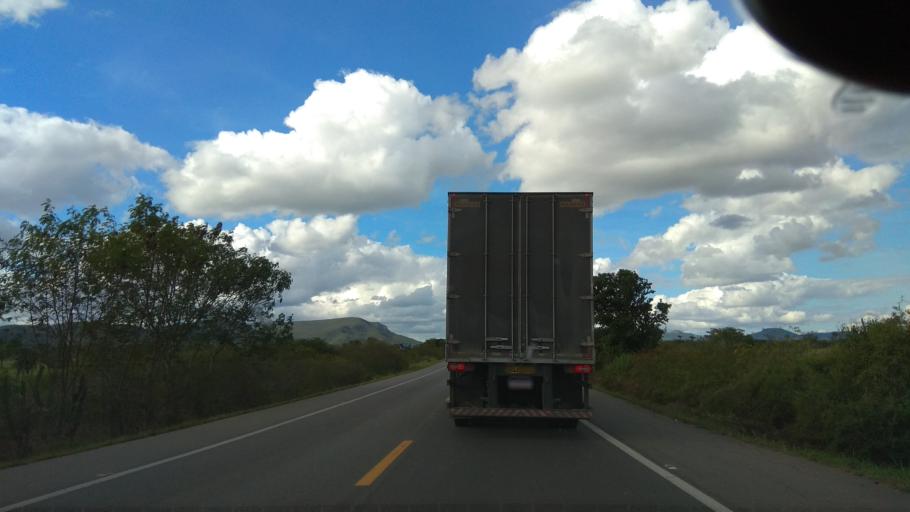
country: BR
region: Bahia
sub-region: Castro Alves
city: Castro Alves
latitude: -12.6758
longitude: -39.6611
